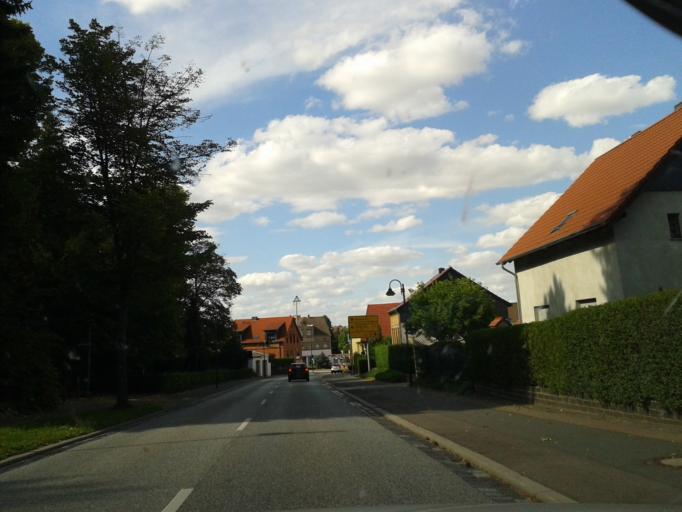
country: DE
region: Saxony-Anhalt
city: Klostermansfeld
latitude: 51.5824
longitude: 11.4938
